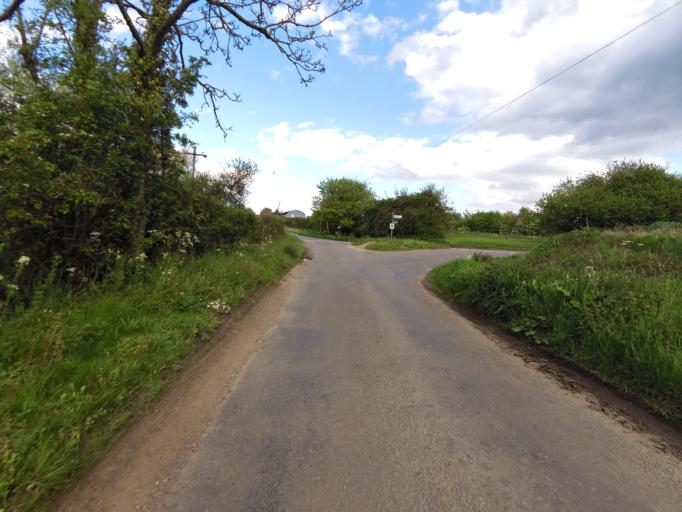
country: GB
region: England
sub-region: Suffolk
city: Elmswell
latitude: 52.2046
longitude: 0.9458
